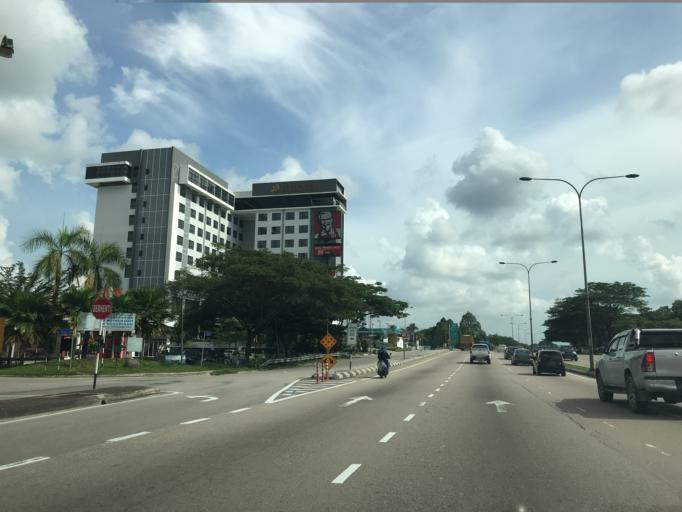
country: MY
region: Johor
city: Taman Senai
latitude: 1.5938
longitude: 103.6466
